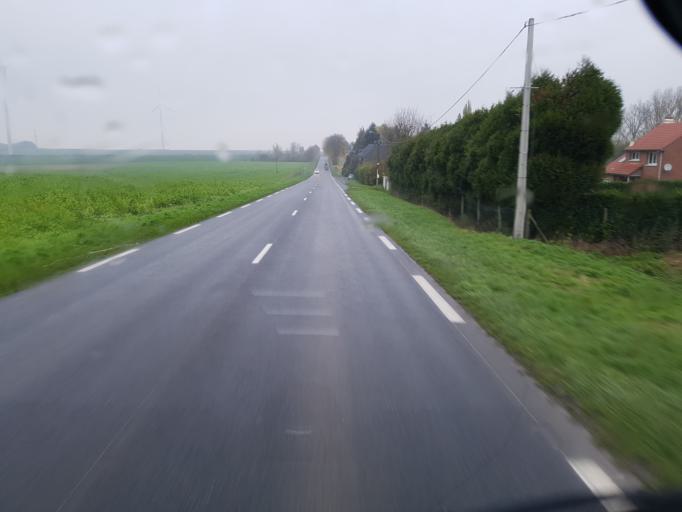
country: FR
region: Picardie
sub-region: Departement de l'Aisne
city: Saint-Quentin
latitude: 49.8927
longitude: 3.2645
